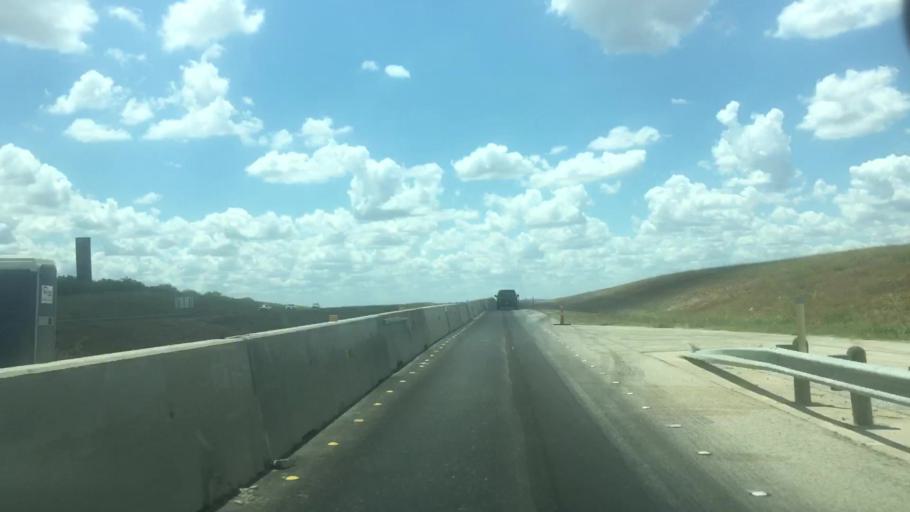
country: US
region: Texas
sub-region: Caldwell County
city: Martindale
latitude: 29.8152
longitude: -97.7619
